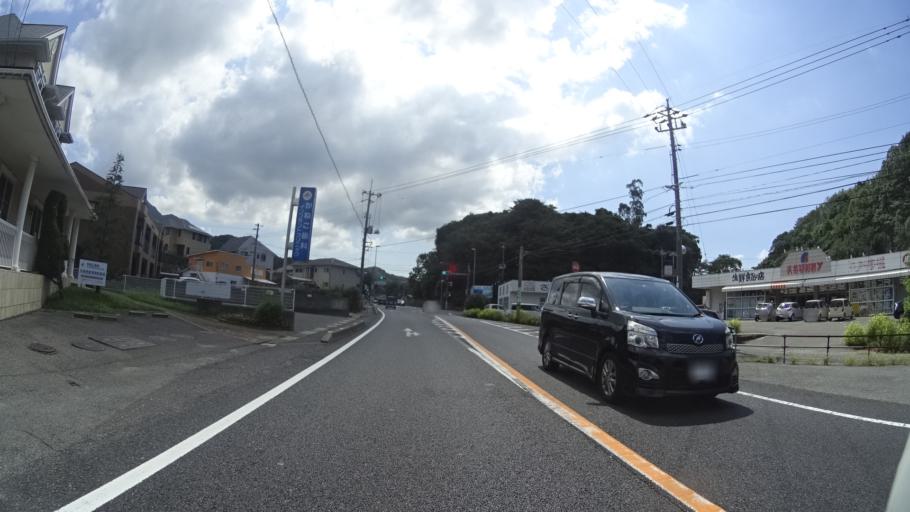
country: JP
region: Yamaguchi
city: Shimonoseki
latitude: 34.0665
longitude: 130.9055
